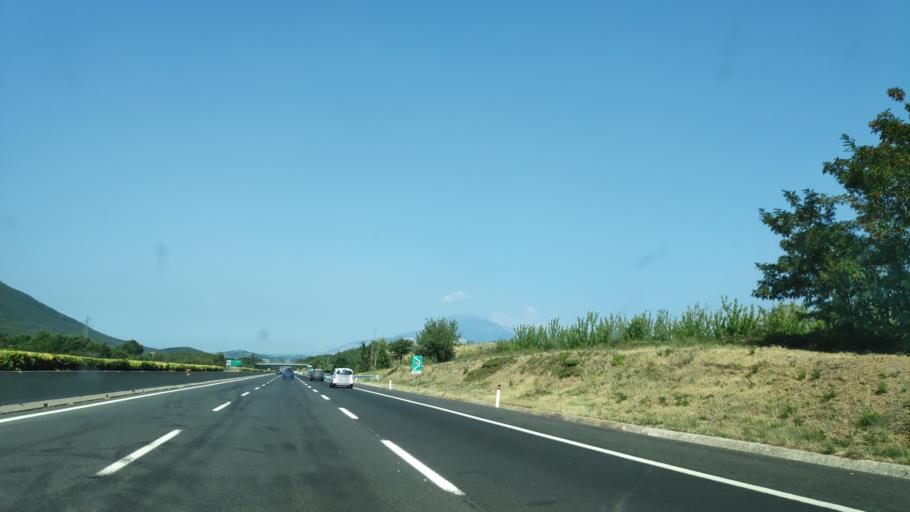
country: IT
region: Campania
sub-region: Provincia di Caserta
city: Mignano Monte Lungo
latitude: 41.4114
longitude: 13.9530
